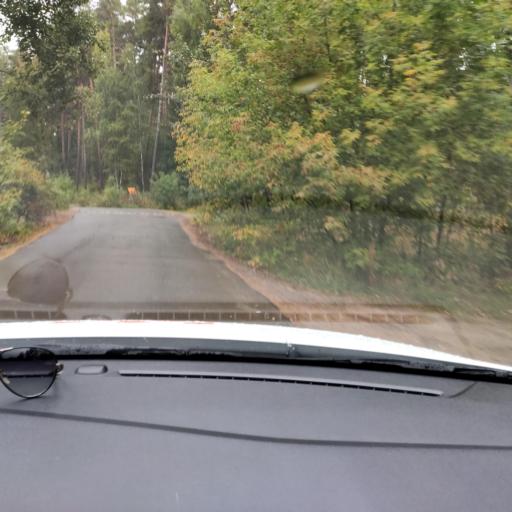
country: RU
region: Tatarstan
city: Verkhniy Uslon
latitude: 55.6430
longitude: 49.0183
